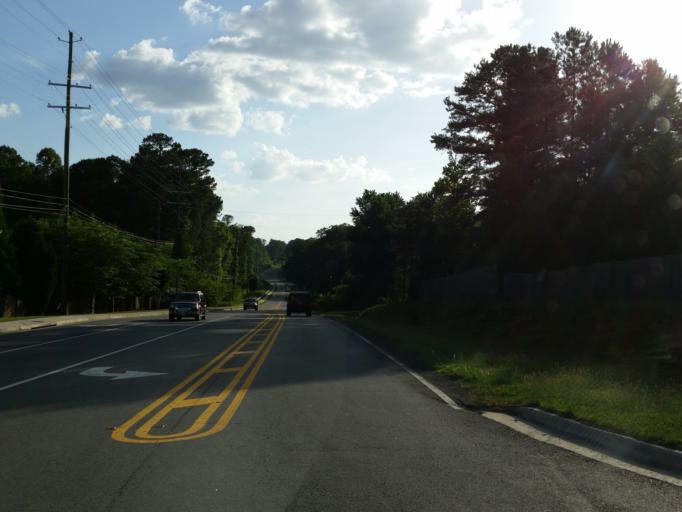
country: US
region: Georgia
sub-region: Cherokee County
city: Woodstock
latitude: 34.0705
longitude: -84.4972
